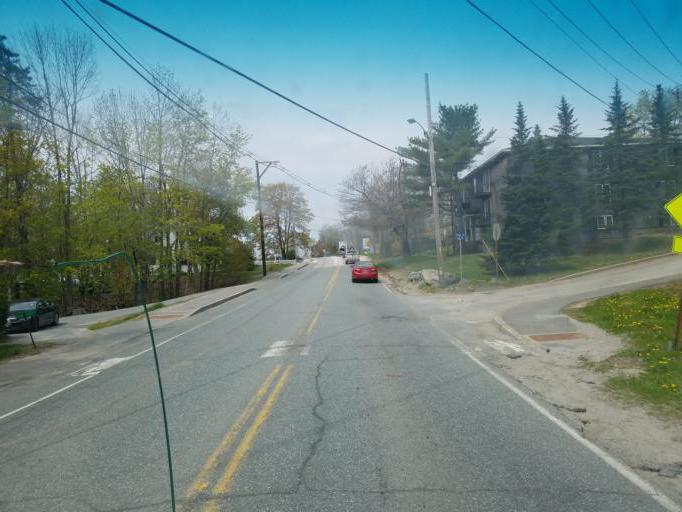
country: US
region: Maine
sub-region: Hancock County
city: Ellsworth
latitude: 44.5483
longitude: -68.4245
